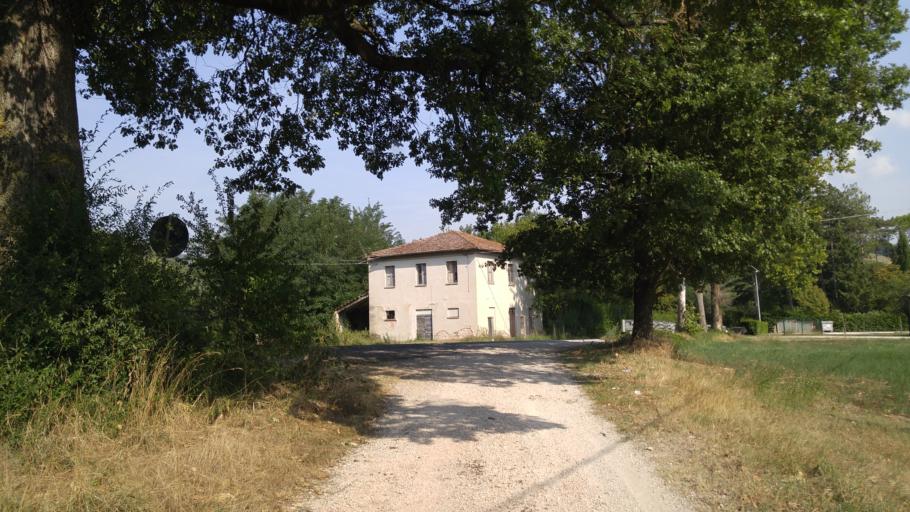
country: IT
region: The Marches
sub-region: Provincia di Pesaro e Urbino
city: Fermignano
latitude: 43.6954
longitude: 12.6682
